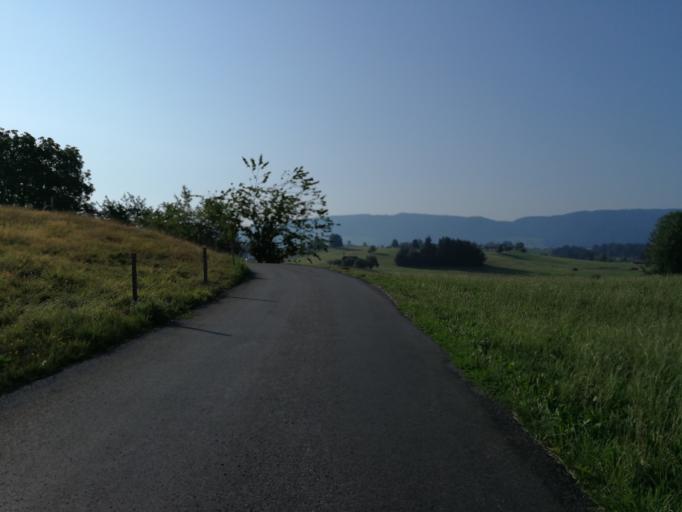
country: CH
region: Zurich
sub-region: Bezirk Horgen
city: Waedenswil / Hangenmoos
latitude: 47.2114
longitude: 8.6292
